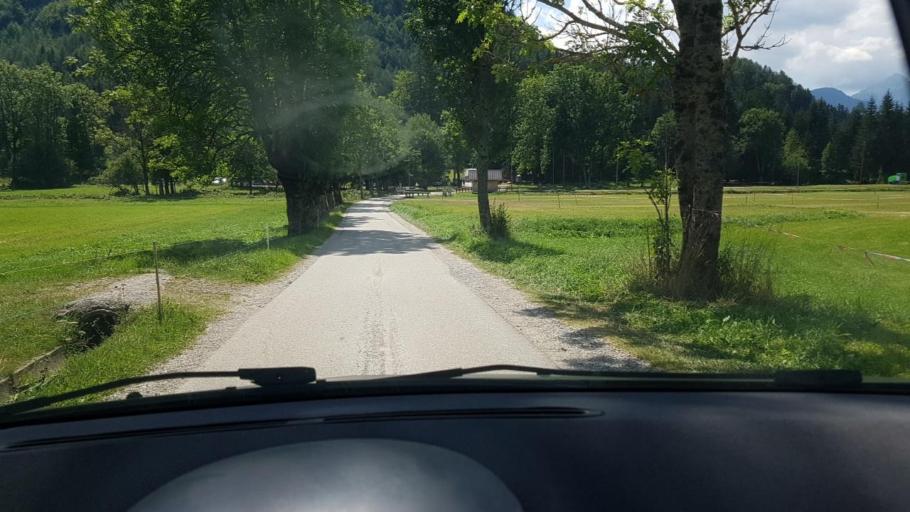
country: SI
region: Jezersko
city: Zgornje Jezersko
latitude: 46.4057
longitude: 14.5163
